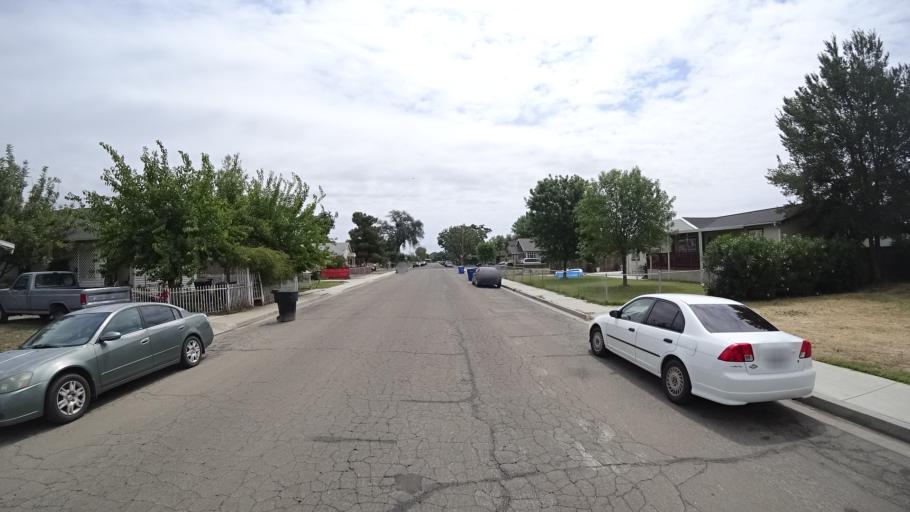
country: US
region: California
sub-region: Kings County
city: Hanford
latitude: 36.3301
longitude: -119.6406
